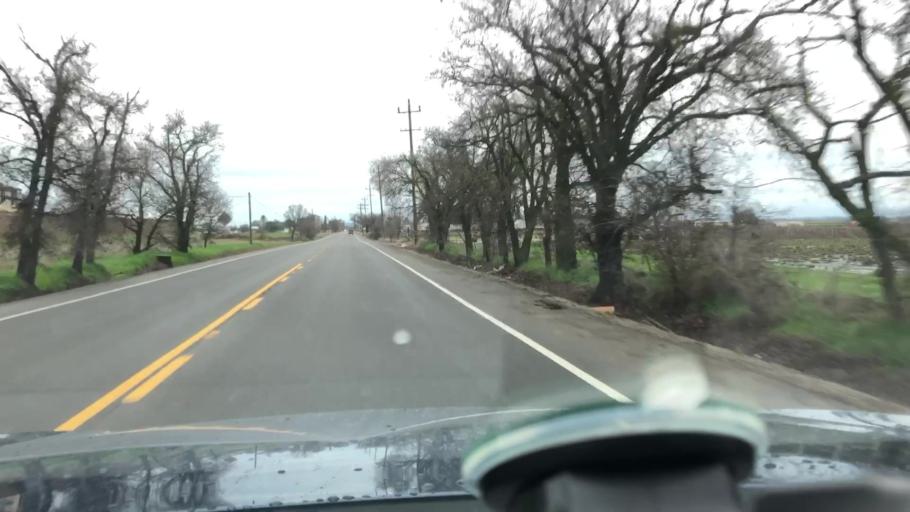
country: US
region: California
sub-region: Sacramento County
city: Elk Grove
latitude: 38.3940
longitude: -121.3408
